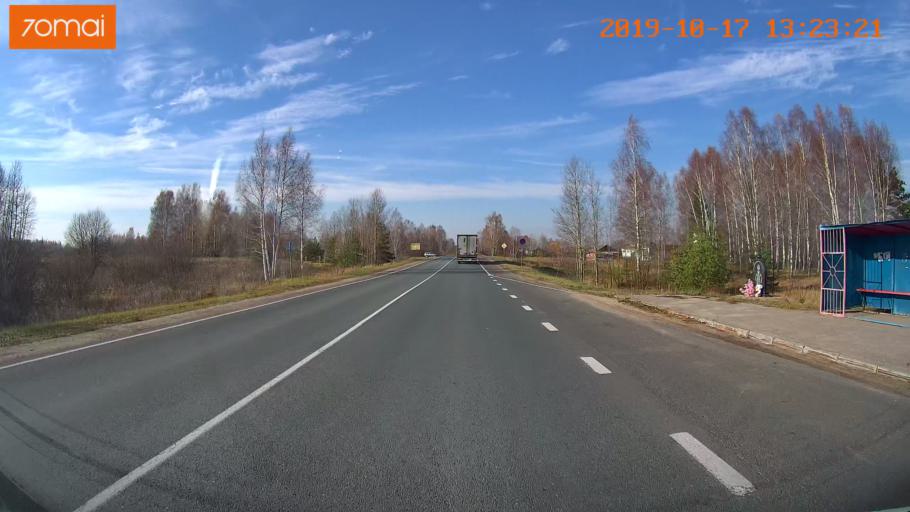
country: RU
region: Rjazan
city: Gus'-Zheleznyy
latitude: 55.0889
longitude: 40.9812
